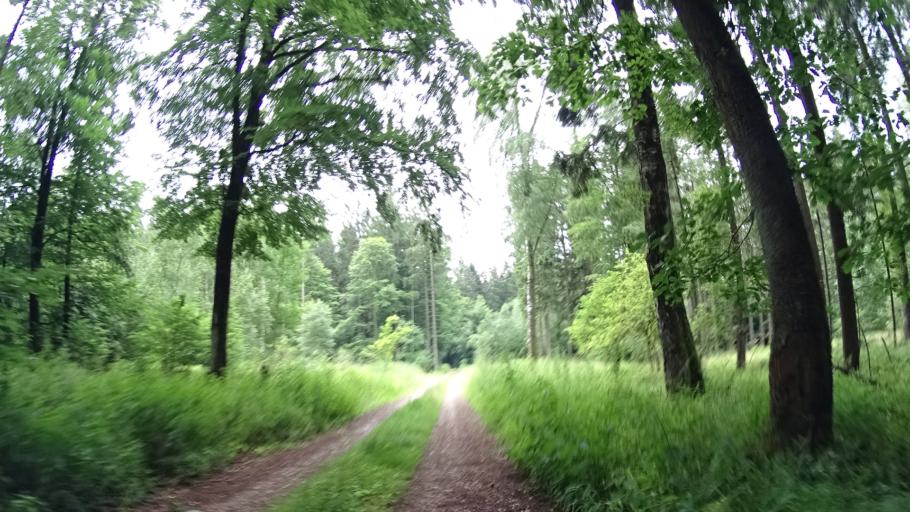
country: DE
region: Bavaria
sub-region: Upper Bavaria
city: Stammham
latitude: 48.8761
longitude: 11.4314
